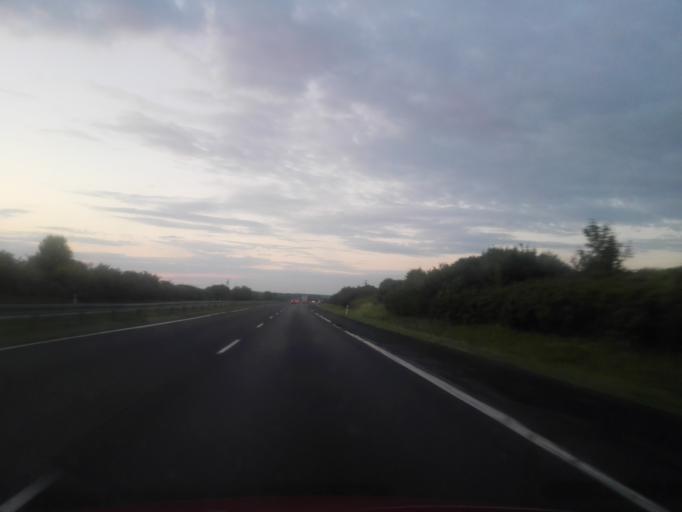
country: PL
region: Lodz Voivodeship
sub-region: Powiat radomszczanski
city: Kamiensk
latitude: 51.2009
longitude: 19.4777
